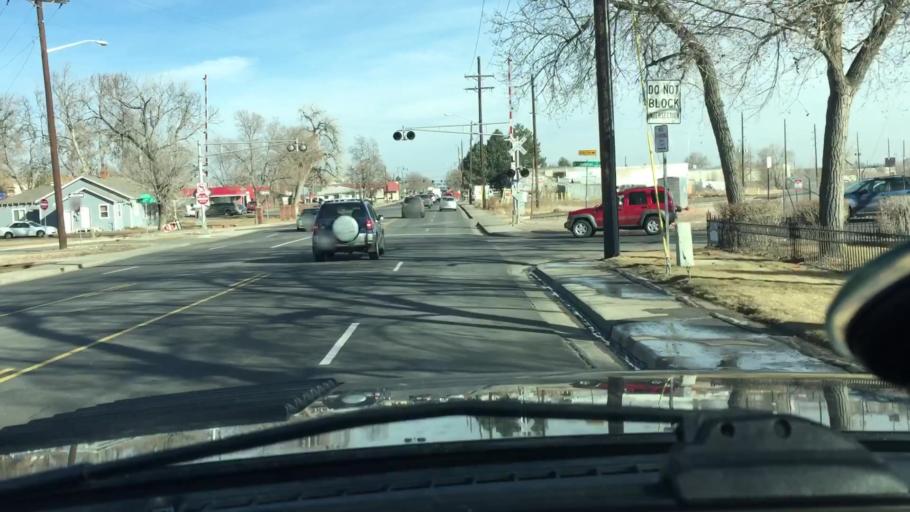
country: US
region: Colorado
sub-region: Adams County
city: Westminster
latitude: 39.8272
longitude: -105.0387
